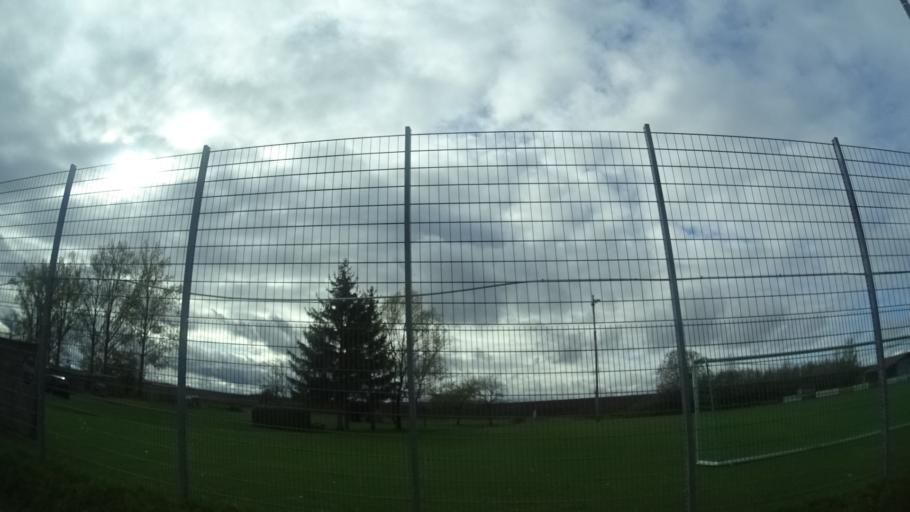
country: DE
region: Bavaria
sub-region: Regierungsbezirk Unterfranken
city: Hochheim
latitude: 50.3863
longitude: 10.4702
